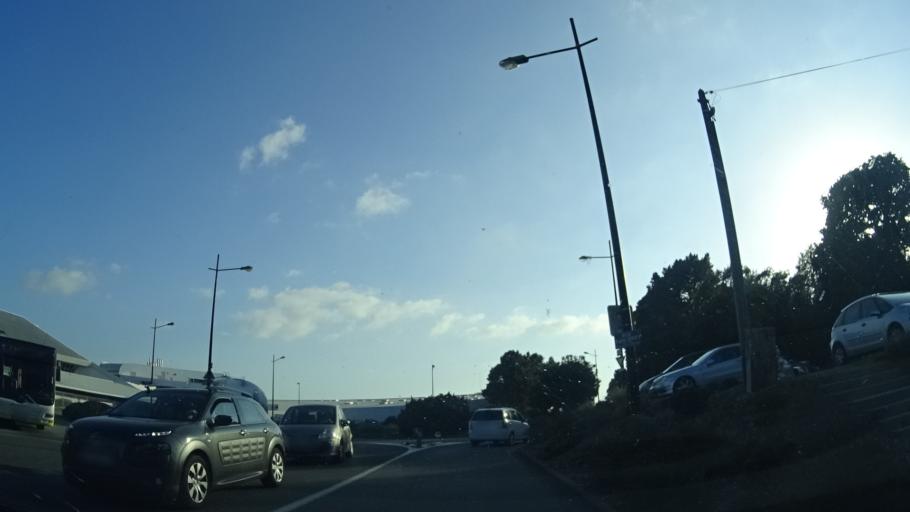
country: FR
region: Brittany
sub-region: Departement du Finistere
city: Le Relecq-Kerhuon
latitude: 48.3912
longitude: -4.4361
